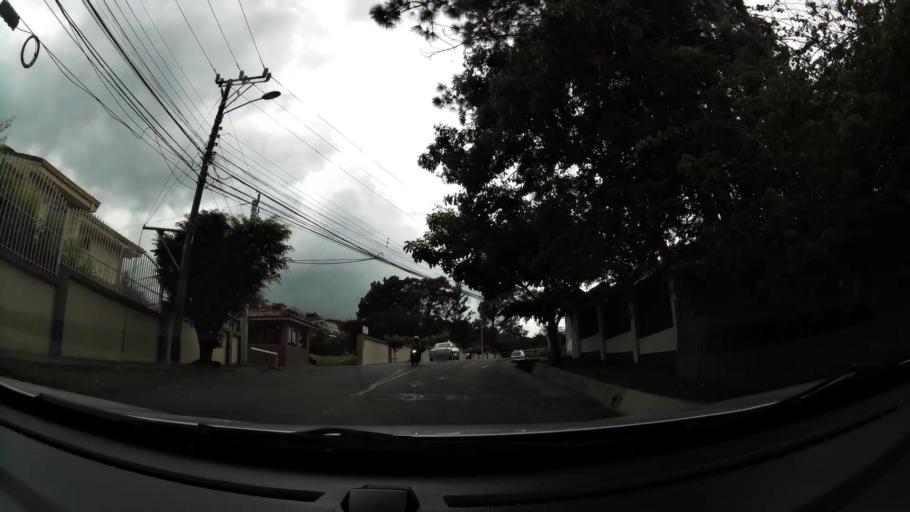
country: CR
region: San Jose
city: San Rafael
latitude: 9.9222
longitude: -84.1231
